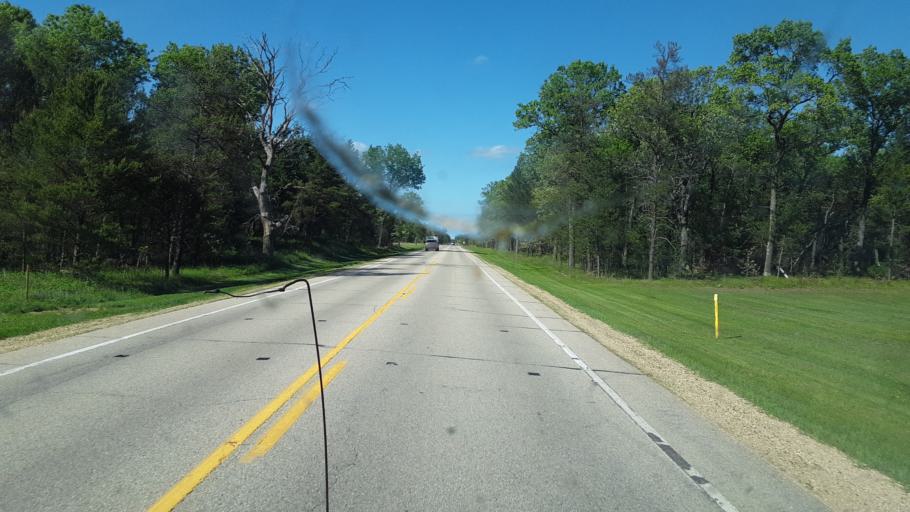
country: US
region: Wisconsin
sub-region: Juneau County
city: New Lisbon
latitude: 43.9492
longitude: -90.0908
